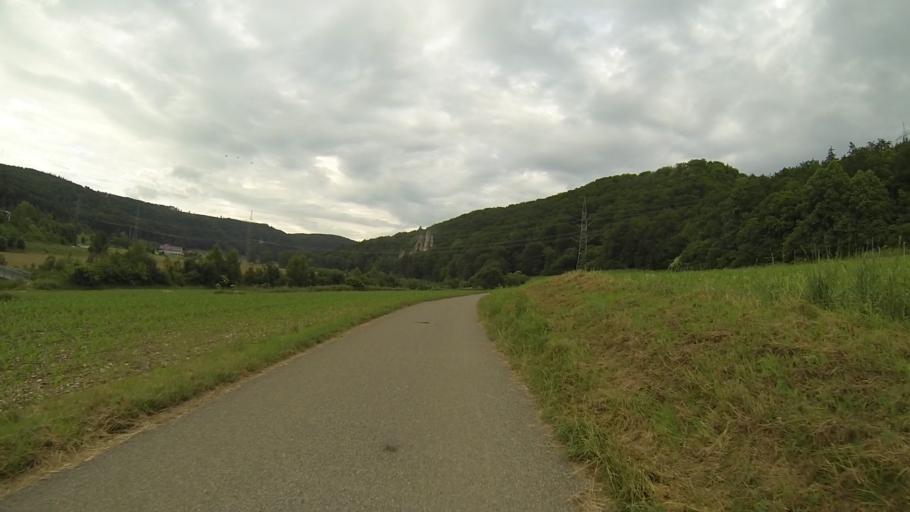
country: DE
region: Baden-Wuerttemberg
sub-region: Tuebingen Region
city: Blaubeuren
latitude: 48.3998
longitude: 9.8293
